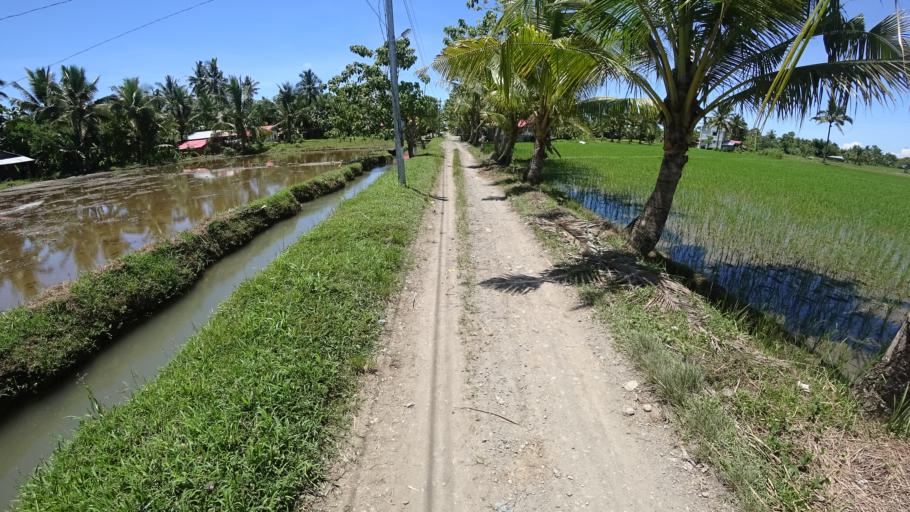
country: PH
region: Eastern Visayas
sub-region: Province of Leyte
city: MacArthur
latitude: 10.8521
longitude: 124.9692
